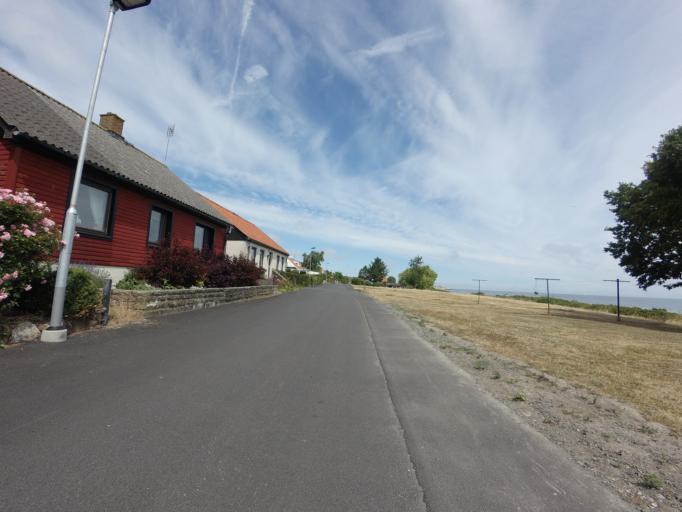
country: SE
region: Skane
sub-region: Simrishamns Kommun
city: Simrishamn
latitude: 55.5445
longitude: 14.3570
